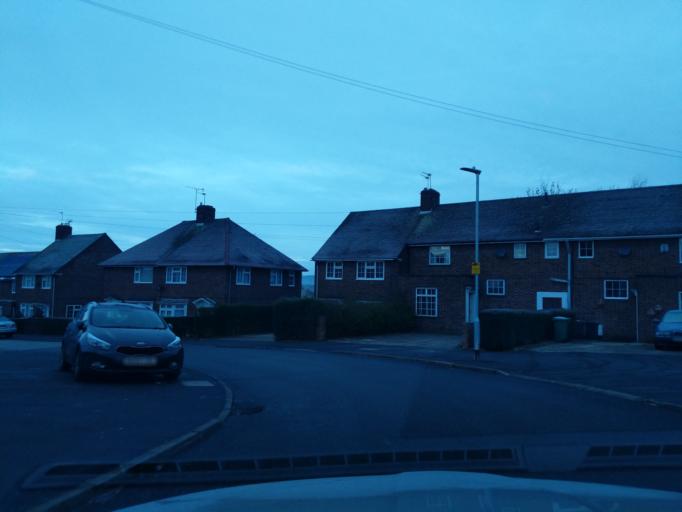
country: GB
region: England
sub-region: Hertfordshire
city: Hemel Hempstead
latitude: 51.7388
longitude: -0.4584
